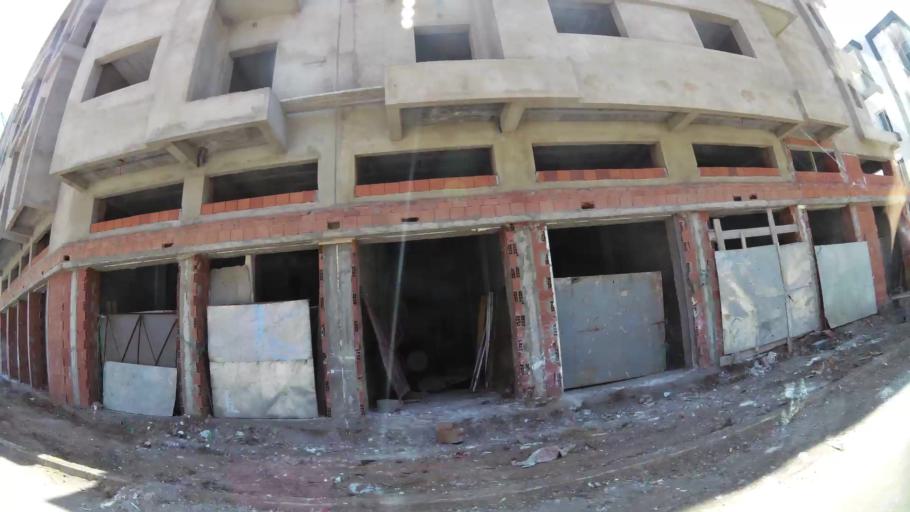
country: MA
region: Gharb-Chrarda-Beni Hssen
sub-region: Kenitra Province
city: Kenitra
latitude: 34.2533
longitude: -6.6119
